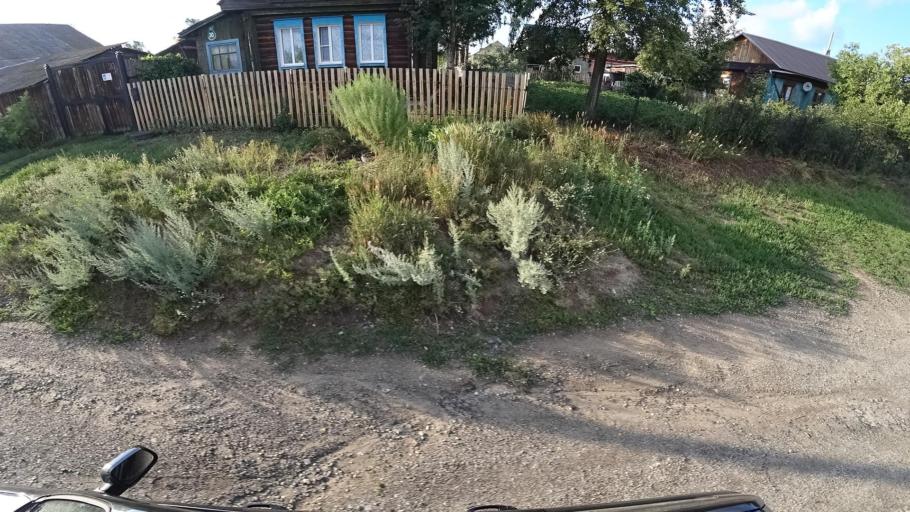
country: RU
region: Sverdlovsk
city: Kamyshlov
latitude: 56.8483
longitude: 62.6661
